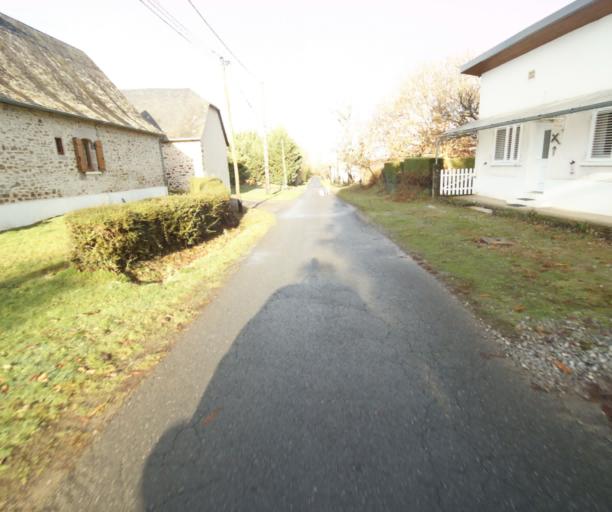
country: FR
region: Limousin
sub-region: Departement de la Correze
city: Saint-Mexant
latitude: 45.2539
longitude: 1.6273
